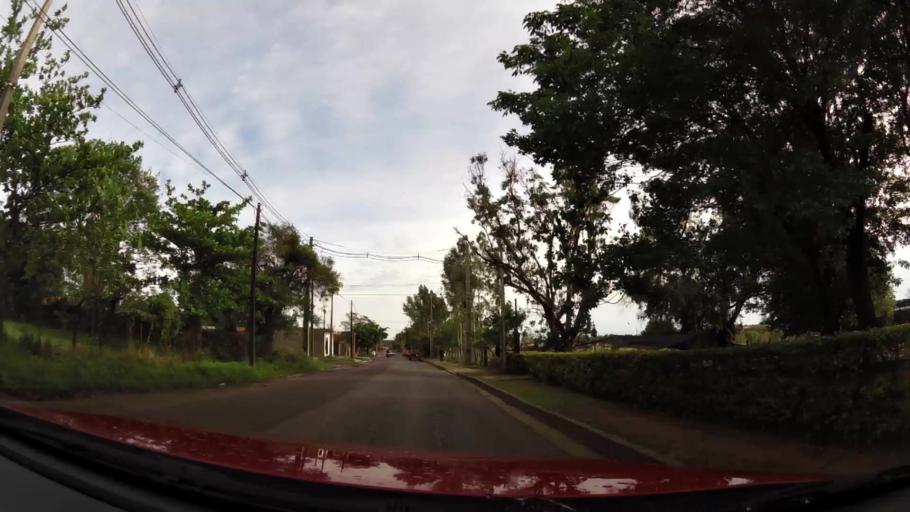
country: PY
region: Central
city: Limpio
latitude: -25.1948
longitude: -57.5033
